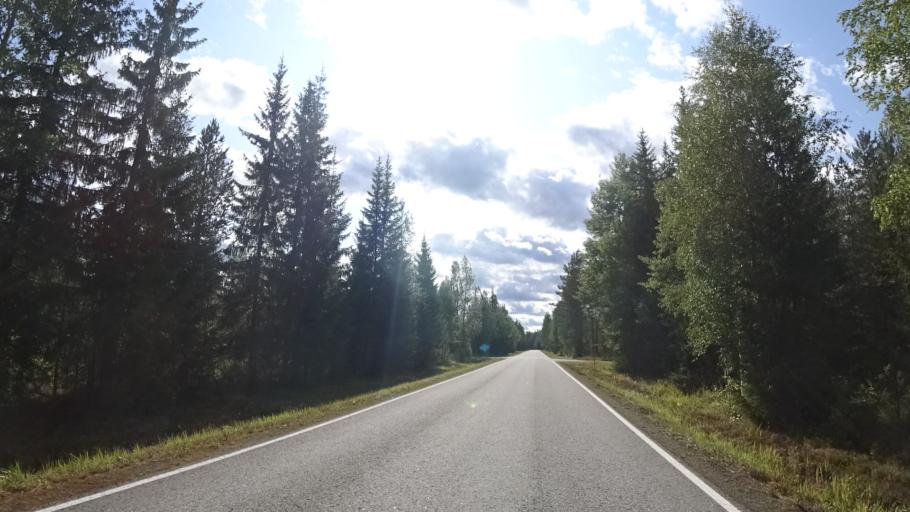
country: RU
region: Republic of Karelia
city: Vyartsilya
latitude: 62.2324
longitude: 30.6831
